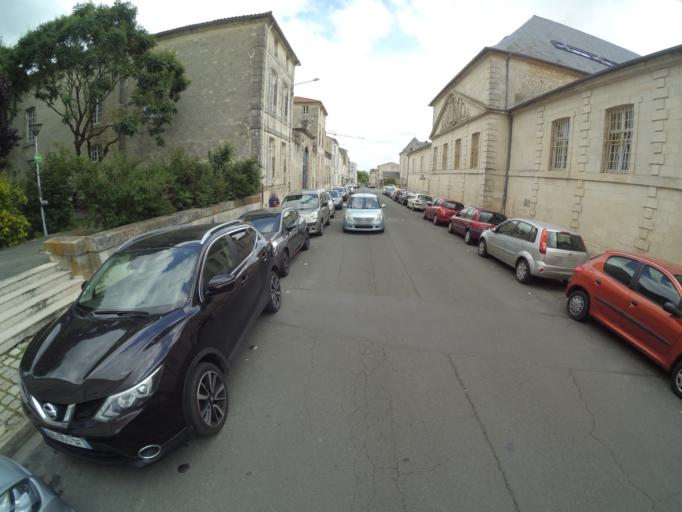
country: FR
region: Poitou-Charentes
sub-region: Departement de la Charente-Maritime
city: Rochefort
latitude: 45.9405
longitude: -0.9593
